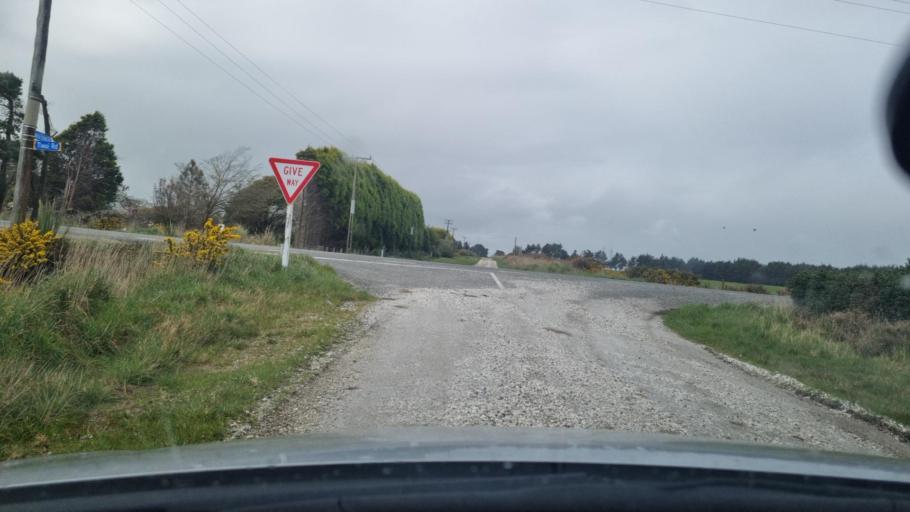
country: NZ
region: Southland
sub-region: Invercargill City
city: Invercargill
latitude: -46.4963
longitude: 168.4188
